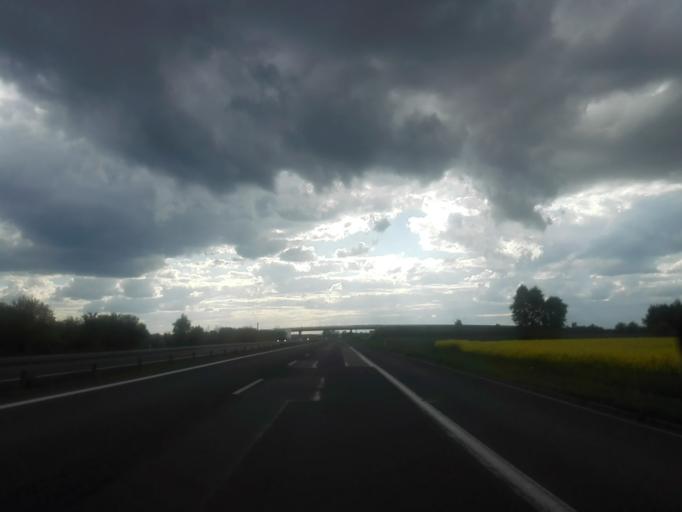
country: PL
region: Masovian Voivodeship
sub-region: Powiat ostrowski
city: Ostrow Mazowiecka
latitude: 52.8206
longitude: 21.9161
